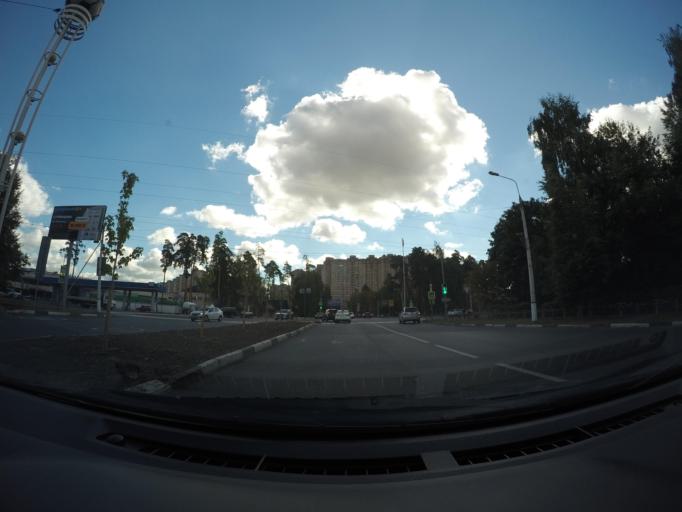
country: RU
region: Moskovskaya
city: Ramenskoye
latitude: 55.5832
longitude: 38.2088
